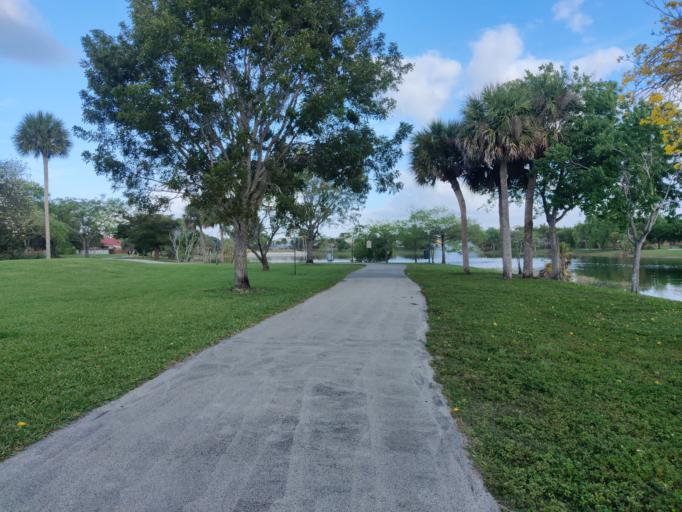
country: US
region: Florida
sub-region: Miami-Dade County
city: The Hammocks
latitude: 25.6660
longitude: -80.4539
